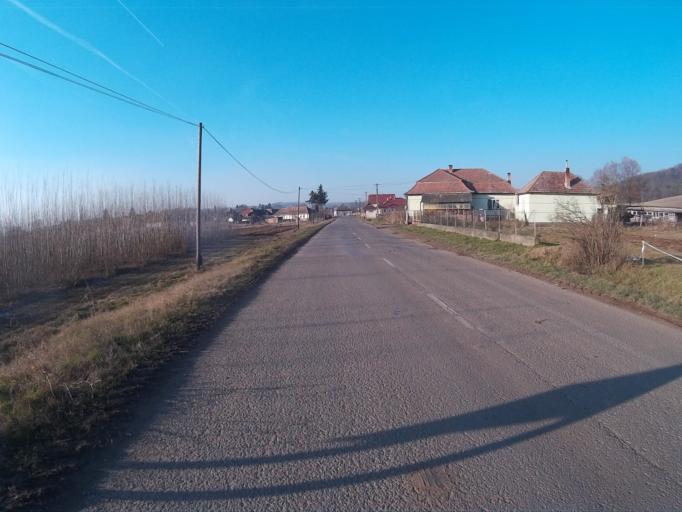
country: HU
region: Nograd
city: Bercel
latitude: 47.9762
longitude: 19.4358
